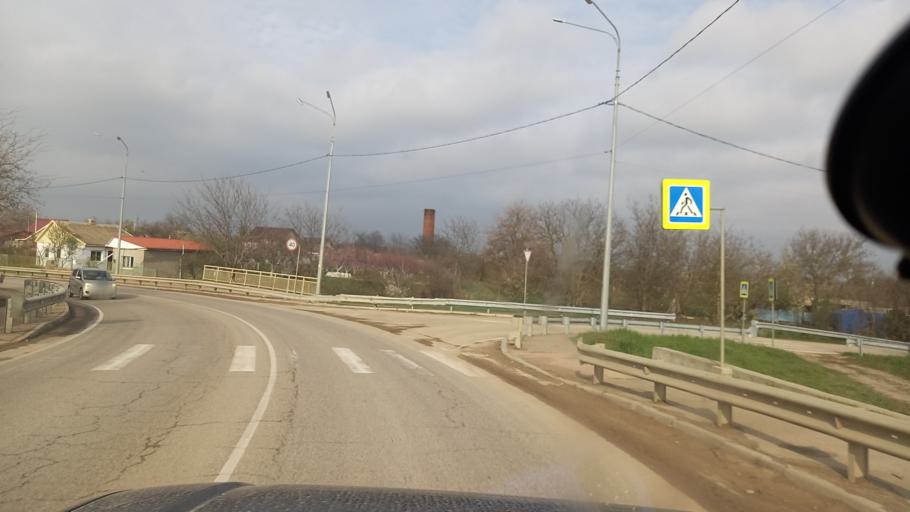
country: RU
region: Krasnodarskiy
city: Varenikovskaya
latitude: 45.1095
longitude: 37.6395
